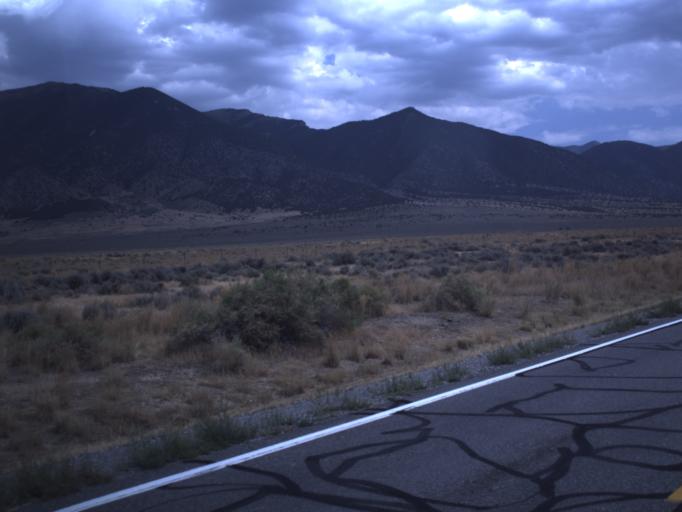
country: US
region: Utah
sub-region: Tooele County
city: Tooele
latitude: 40.3661
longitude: -112.3441
